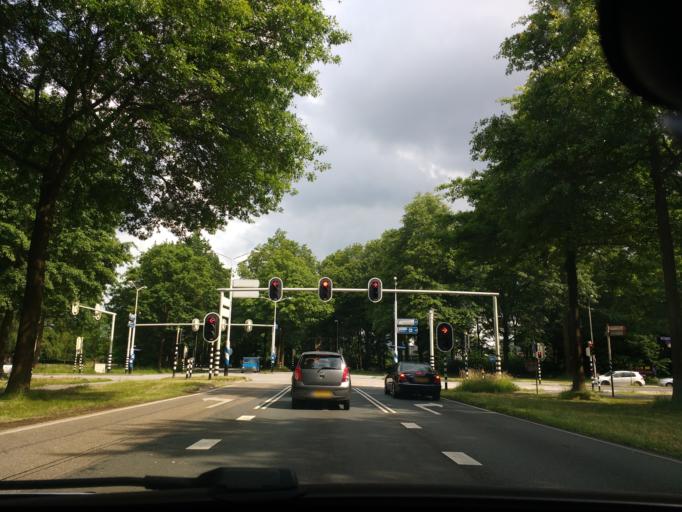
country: NL
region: Gelderland
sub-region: Gemeente Wageningen
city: Wageningen
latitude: 51.9823
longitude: 5.6741
